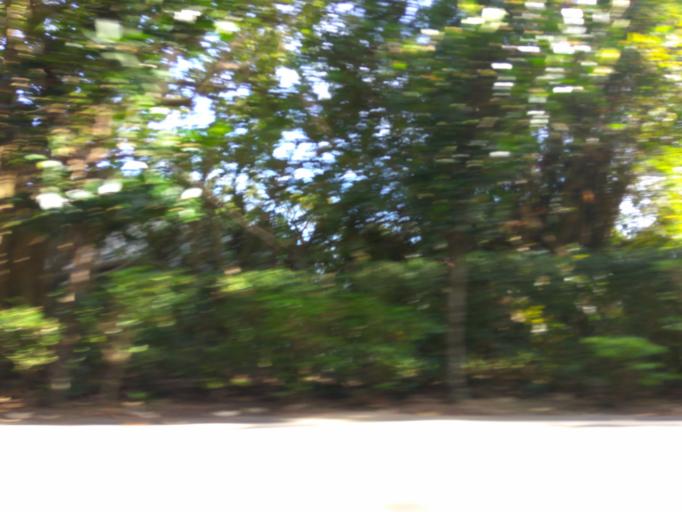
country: TW
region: Taiwan
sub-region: Hsinchu
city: Zhubei
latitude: 24.9682
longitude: 121.0111
